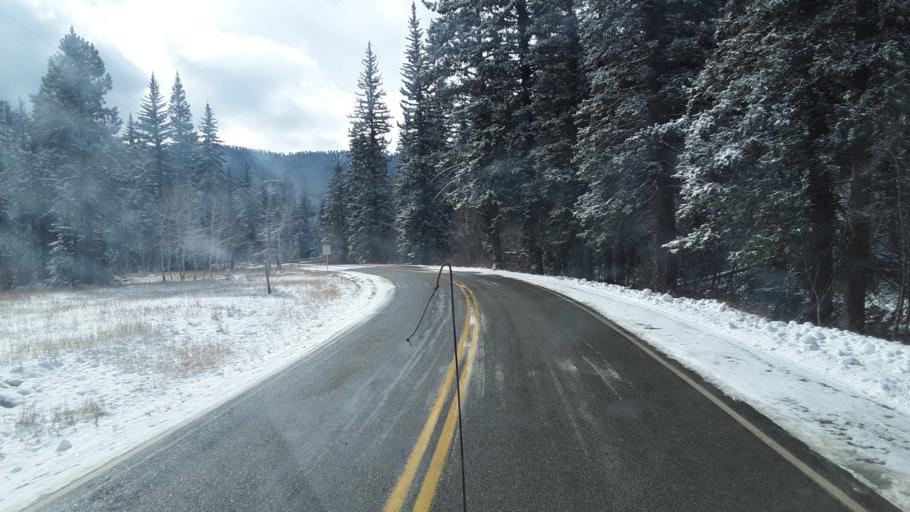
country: US
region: Colorado
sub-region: La Plata County
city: Bayfield
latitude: 37.3694
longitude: -107.6661
